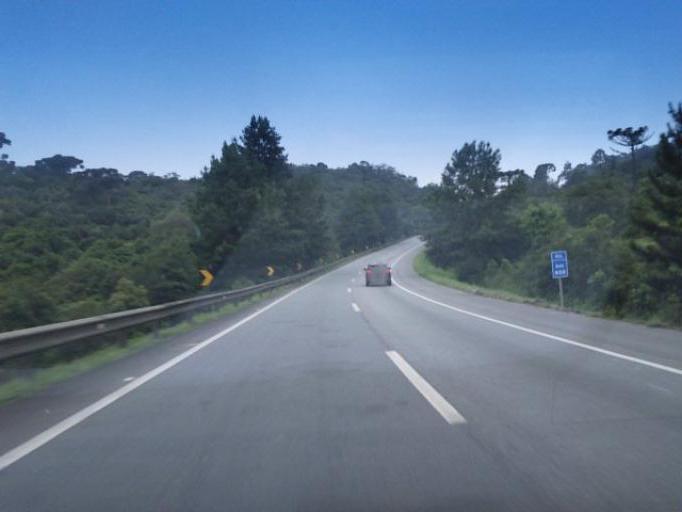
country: BR
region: Parana
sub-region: Sao Jose Dos Pinhais
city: Sao Jose dos Pinhais
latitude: -25.8495
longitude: -49.0147
